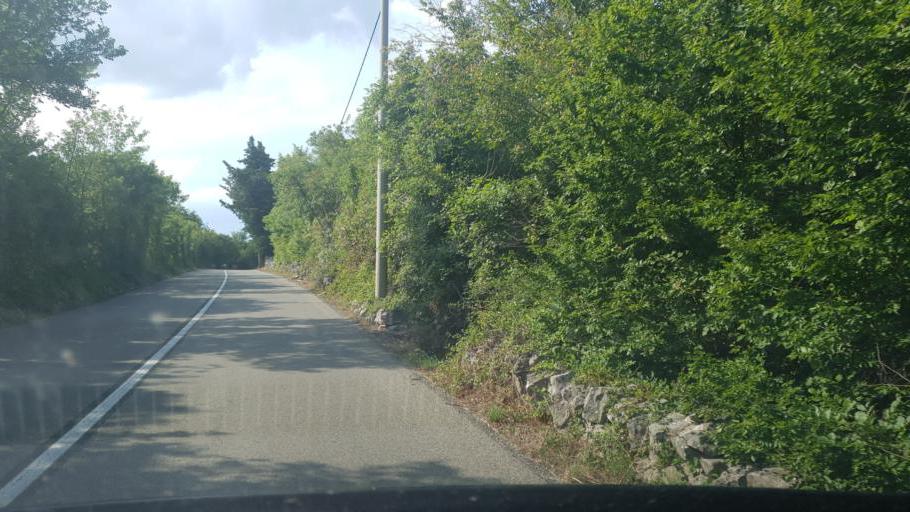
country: HR
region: Primorsko-Goranska
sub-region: Grad Crikvenica
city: Crikvenica
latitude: 45.1222
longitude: 14.6266
